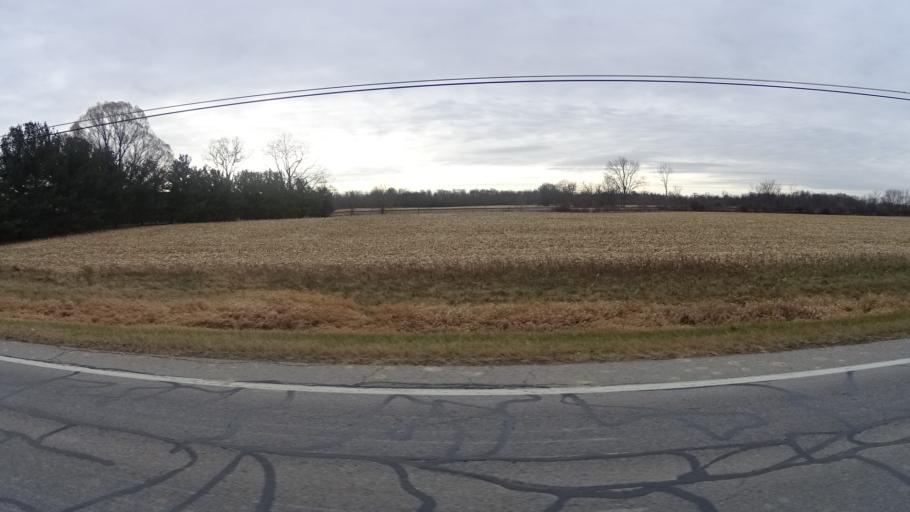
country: US
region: Ohio
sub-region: Lorain County
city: Wellington
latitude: 41.1693
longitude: -82.2586
